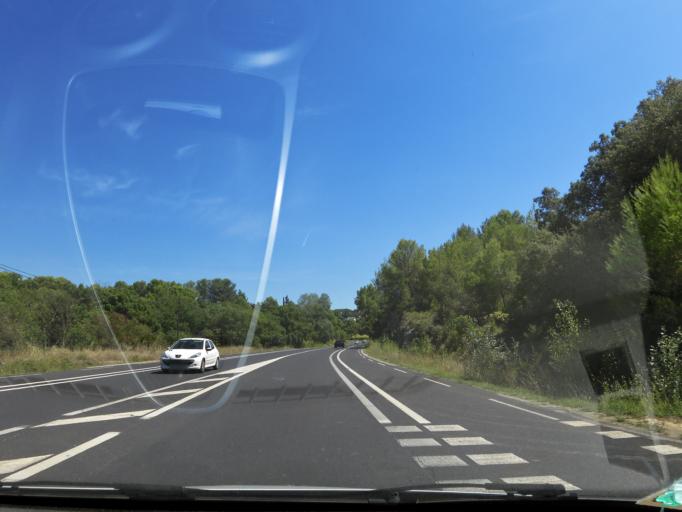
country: FR
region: Languedoc-Roussillon
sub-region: Departement de l'Herault
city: Clapiers
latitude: 43.6464
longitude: 3.8888
